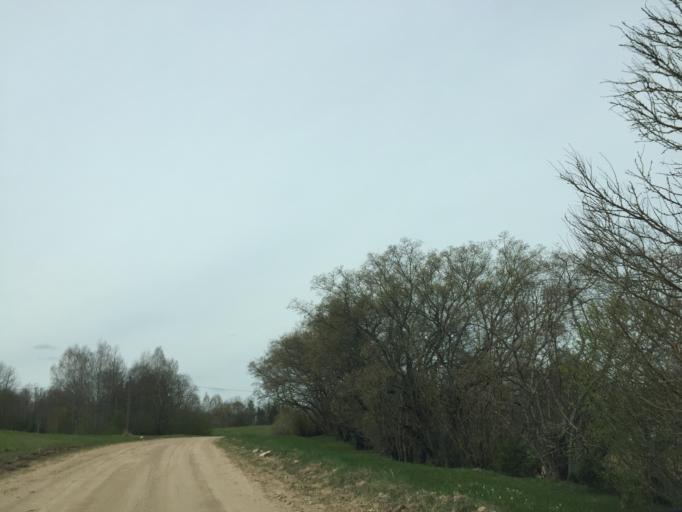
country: LV
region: Ludzas Rajons
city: Ludza
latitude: 56.5119
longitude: 27.5605
